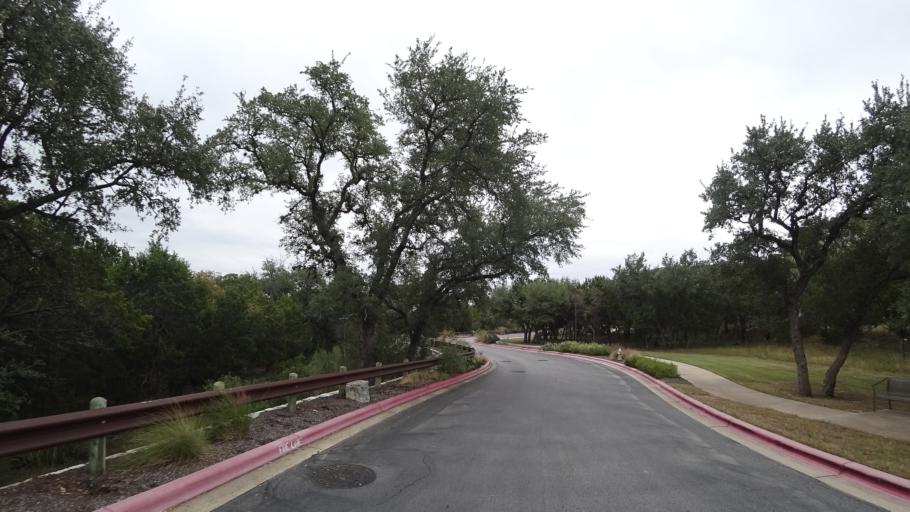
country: US
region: Texas
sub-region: Travis County
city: Bee Cave
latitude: 30.3523
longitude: -97.9094
